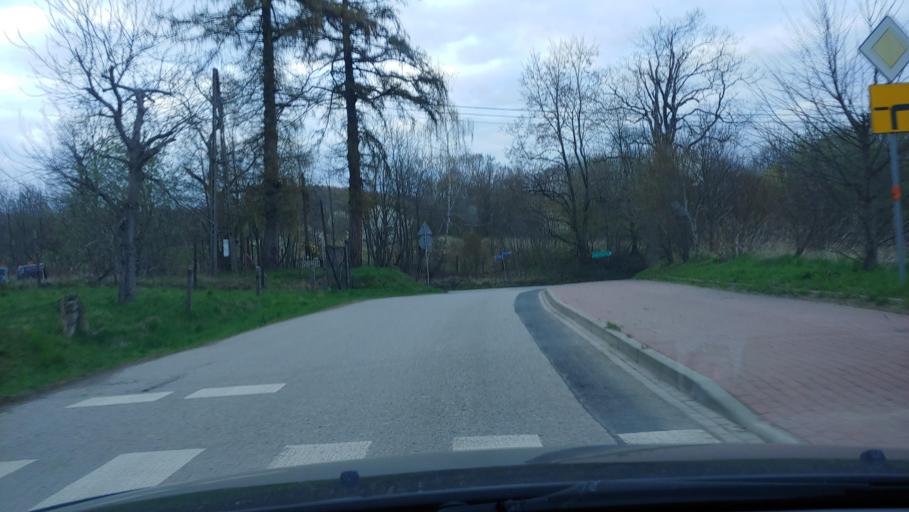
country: PL
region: Lesser Poland Voivodeship
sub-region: Powiat krakowski
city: Bolechowice
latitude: 50.1475
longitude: 19.7521
